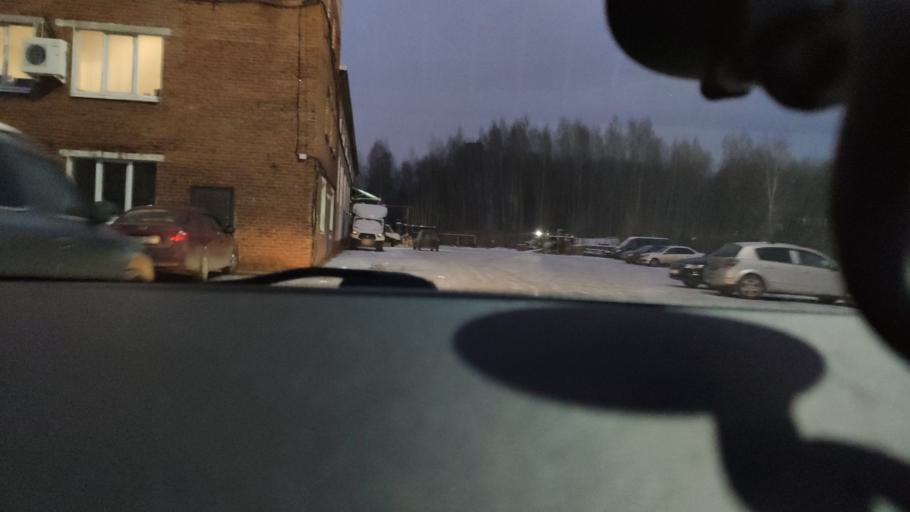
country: RU
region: Perm
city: Froly
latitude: 57.9645
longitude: 56.2729
